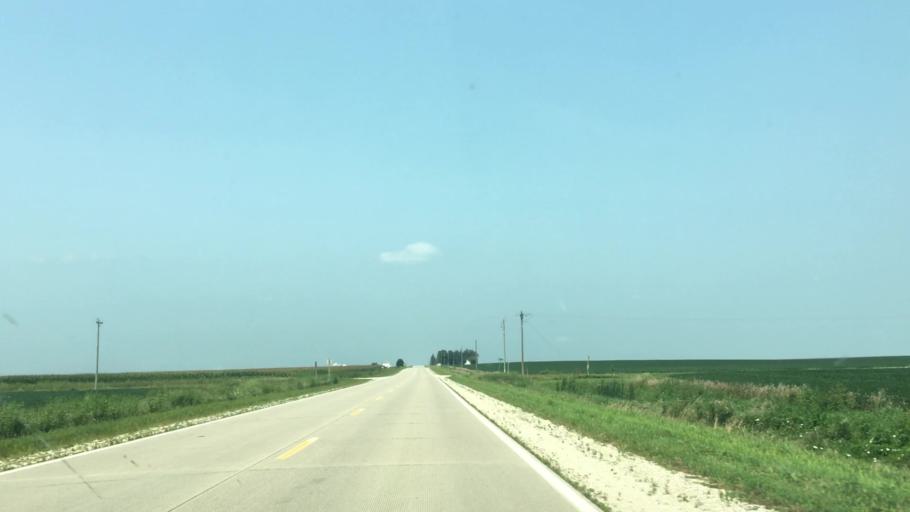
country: US
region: Iowa
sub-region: Fayette County
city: Oelwein
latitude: 42.7009
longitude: -91.8049
